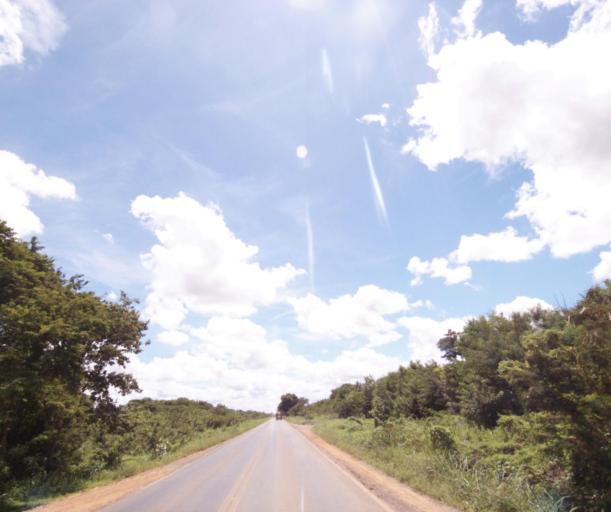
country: BR
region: Bahia
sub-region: Bom Jesus Da Lapa
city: Bom Jesus da Lapa
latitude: -13.2636
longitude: -43.5560
